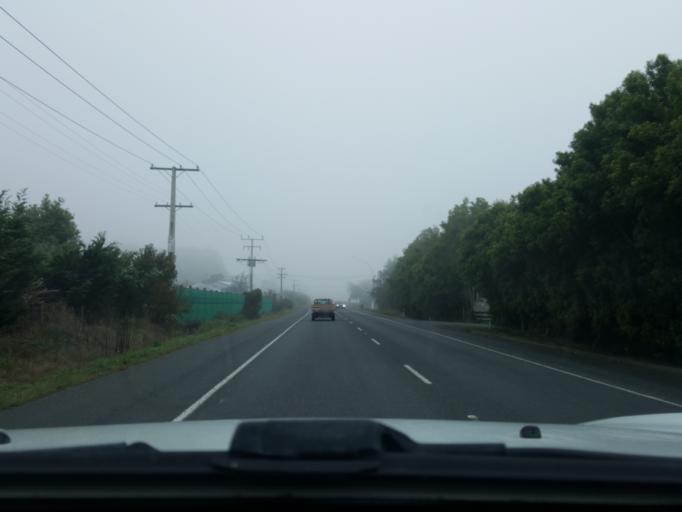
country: NZ
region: Waikato
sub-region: Waikato District
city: Ngaruawahia
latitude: -37.6932
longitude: 175.1873
